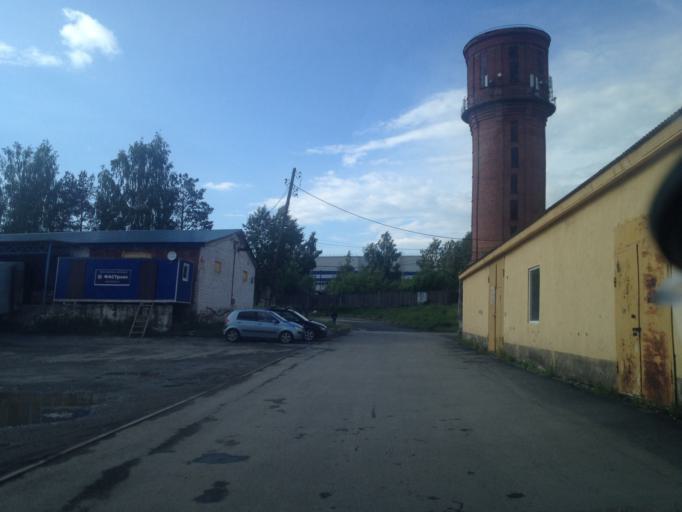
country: RU
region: Sverdlovsk
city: Yekaterinburg
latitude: 56.9111
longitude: 60.6335
